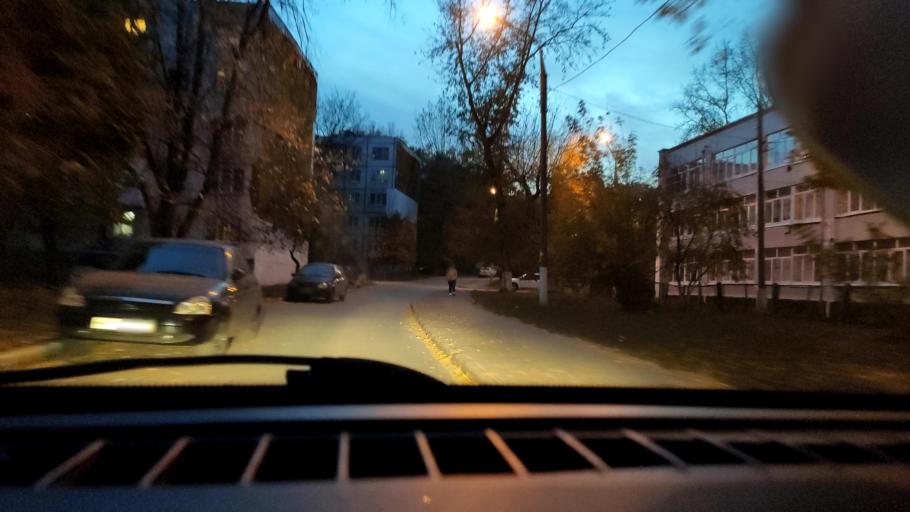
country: RU
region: Samara
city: Petra-Dubrava
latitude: 53.2509
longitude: 50.2640
